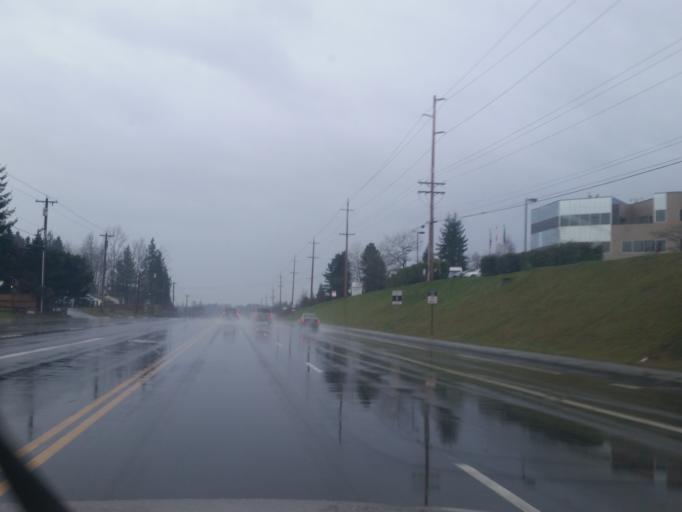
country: US
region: Washington
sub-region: Snohomish County
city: Martha Lake
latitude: 47.8962
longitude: -122.2634
